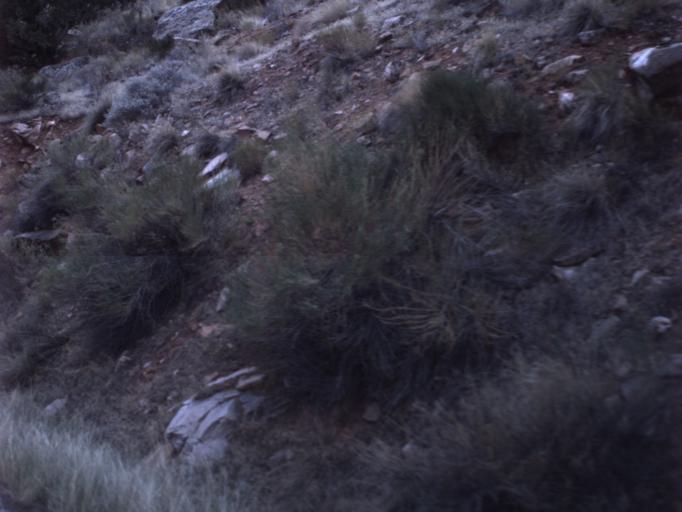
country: US
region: Utah
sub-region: Grand County
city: Moab
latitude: 38.7982
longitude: -109.3321
